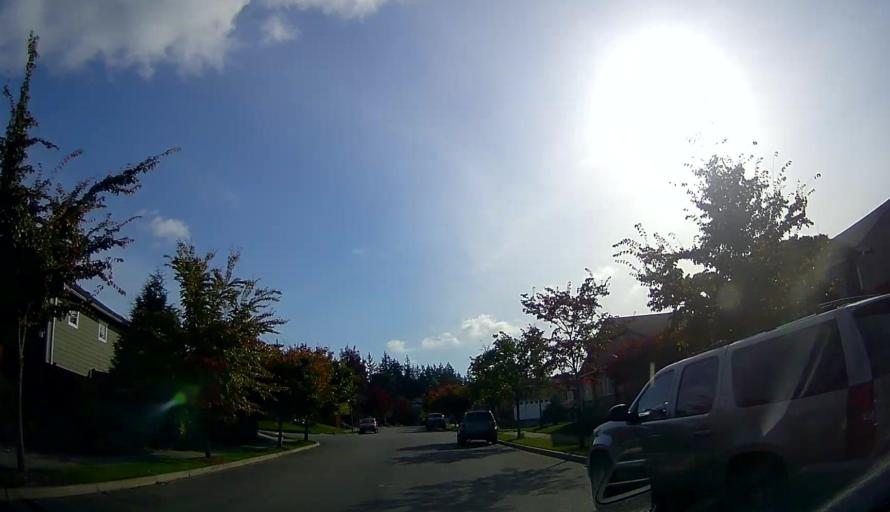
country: US
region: Washington
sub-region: Skagit County
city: Mount Vernon
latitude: 48.4194
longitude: -122.2950
